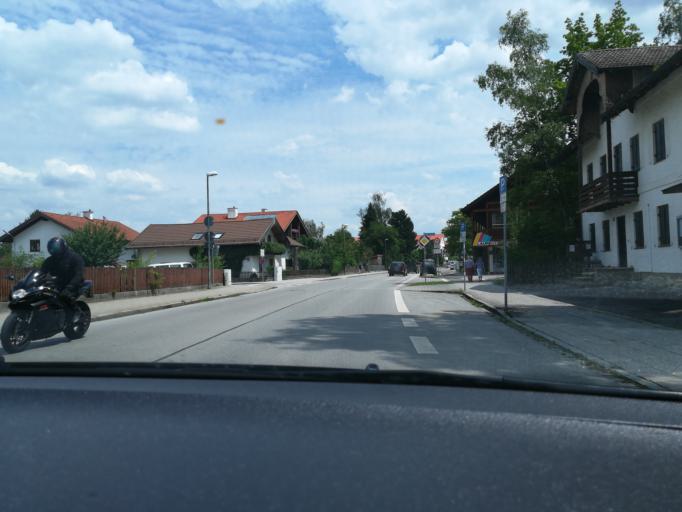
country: DE
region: Bavaria
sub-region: Upper Bavaria
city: Hohenkirchen-Siegertsbrunn
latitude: 48.0200
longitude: 11.7220
